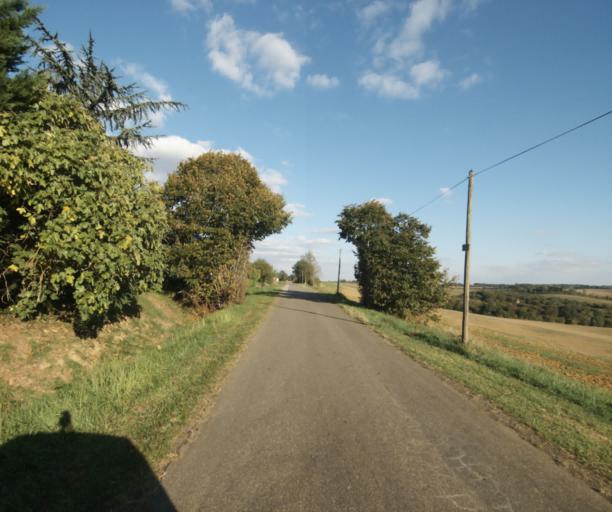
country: FR
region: Midi-Pyrenees
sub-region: Departement du Gers
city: Eauze
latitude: 43.7488
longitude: 0.1245
